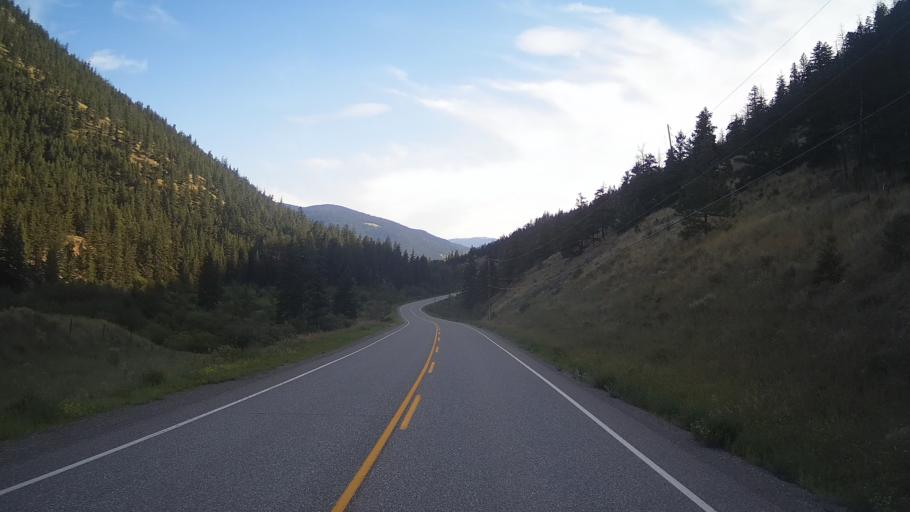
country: CA
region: British Columbia
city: Cache Creek
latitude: 50.8744
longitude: -121.5196
